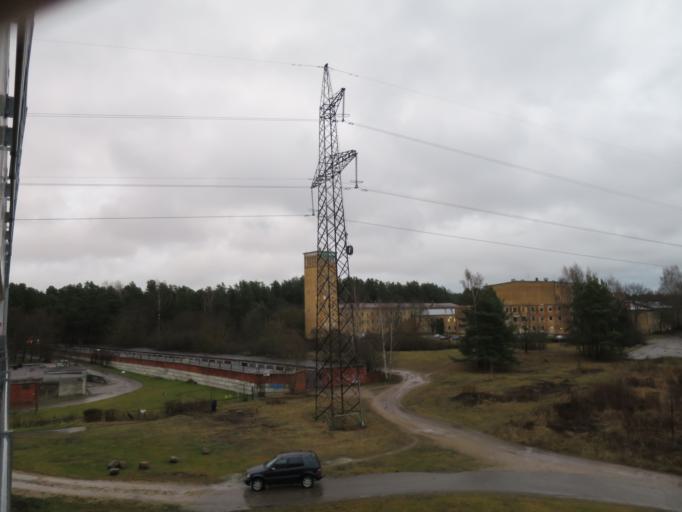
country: LV
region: Riga
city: Jaunciems
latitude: 56.9813
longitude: 24.2062
